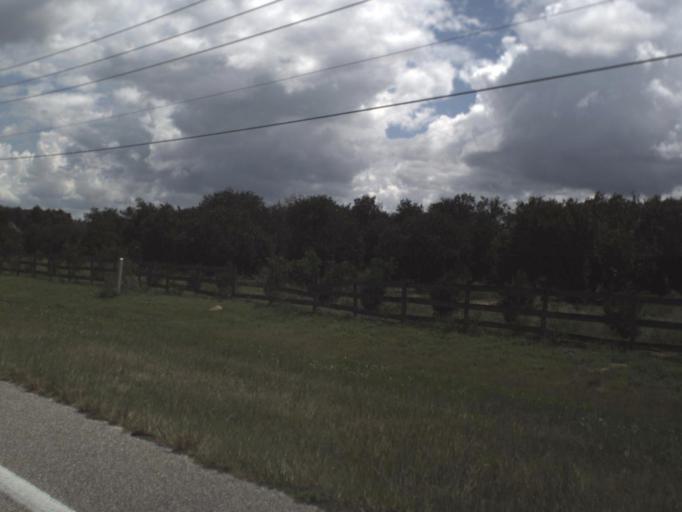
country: US
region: Florida
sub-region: Polk County
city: Babson Park
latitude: 27.8874
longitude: -81.4681
